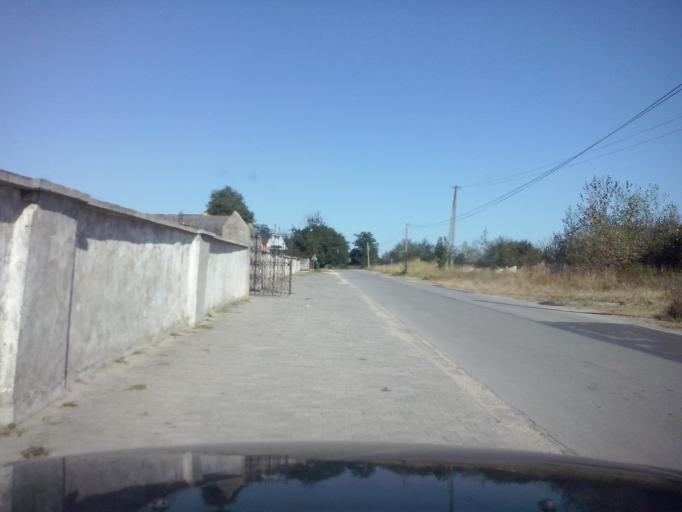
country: PL
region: Swietokrzyskie
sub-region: Powiat pinczowski
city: Kije
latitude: 50.5783
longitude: 20.6618
